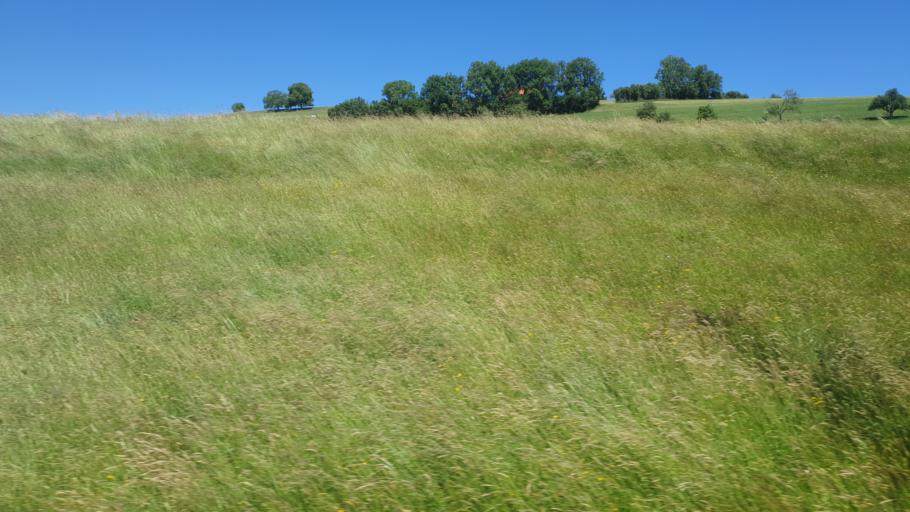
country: CH
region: Fribourg
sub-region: Sarine District
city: Givisiez
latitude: 46.8395
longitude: 7.1319
